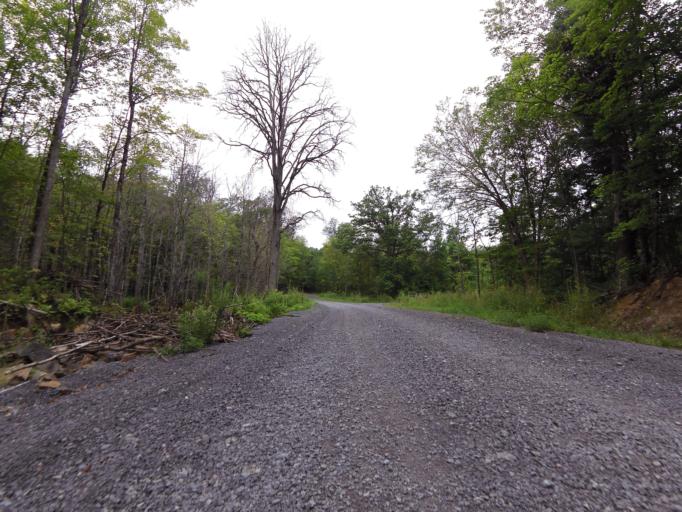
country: CA
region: Ontario
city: Perth
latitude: 44.7014
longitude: -76.6391
